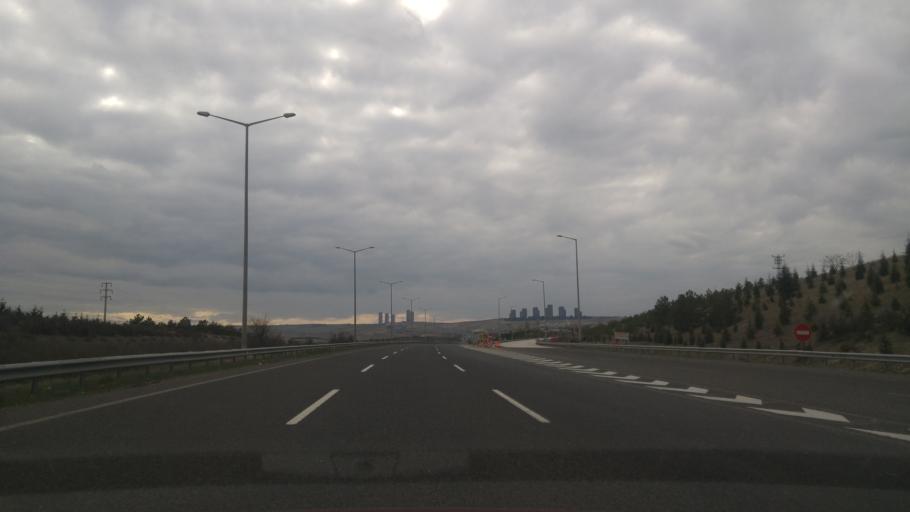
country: TR
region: Ankara
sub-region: Goelbasi
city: Golbasi
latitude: 39.7865
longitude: 32.7666
